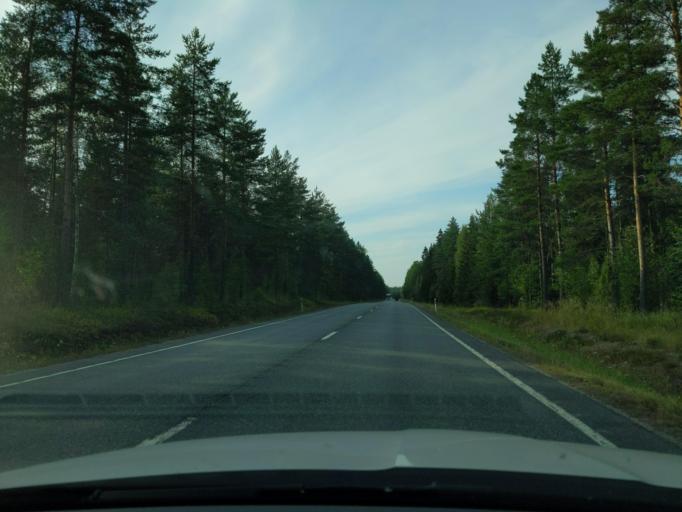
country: FI
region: Paijanne Tavastia
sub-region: Lahti
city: Padasjoki
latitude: 61.2916
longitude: 25.3093
